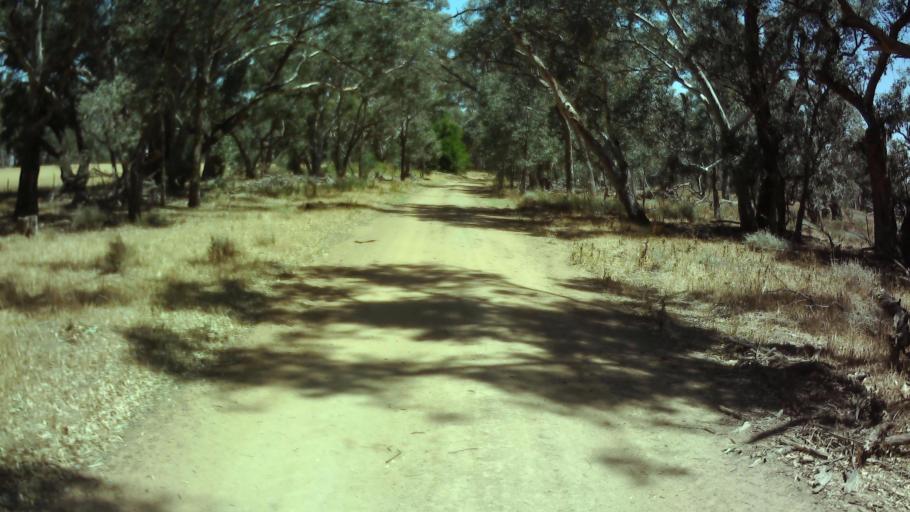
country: AU
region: New South Wales
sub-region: Weddin
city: Grenfell
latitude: -34.0452
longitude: 147.8385
